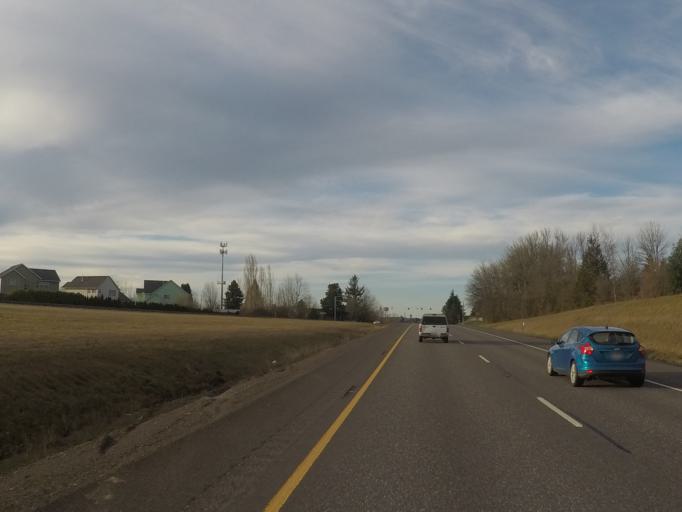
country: US
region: Oregon
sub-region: Multnomah County
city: Gresham
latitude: 45.4748
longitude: -122.3962
